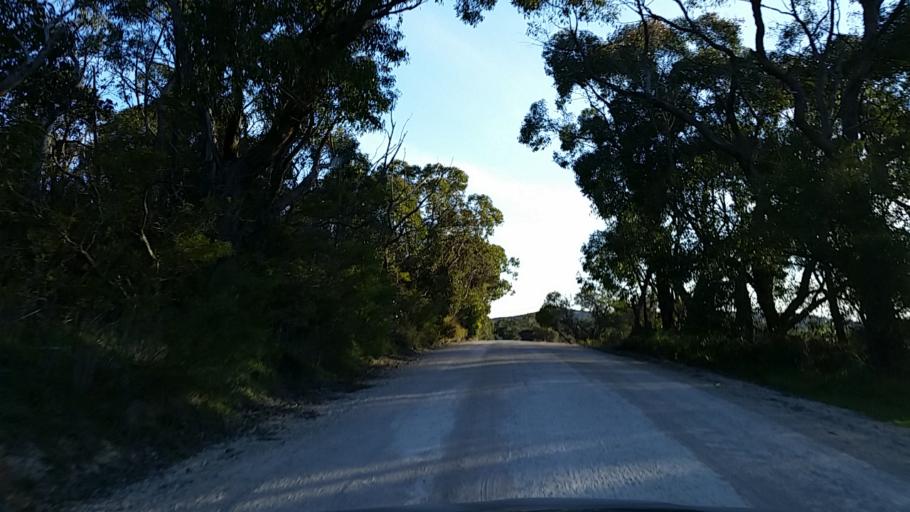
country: AU
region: South Australia
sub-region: Alexandrina
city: Mount Compass
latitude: -35.3046
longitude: 138.6766
